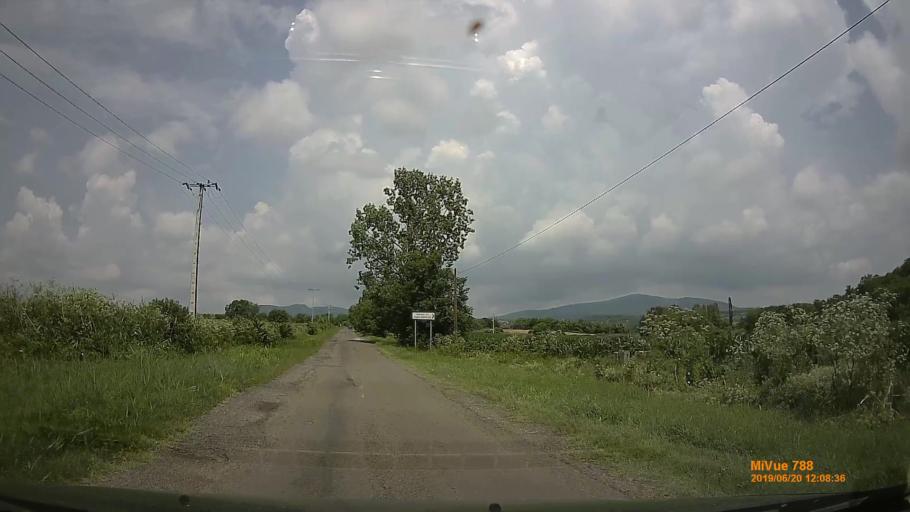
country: HU
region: Baranya
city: Hosszuheteny
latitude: 46.1293
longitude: 18.3673
